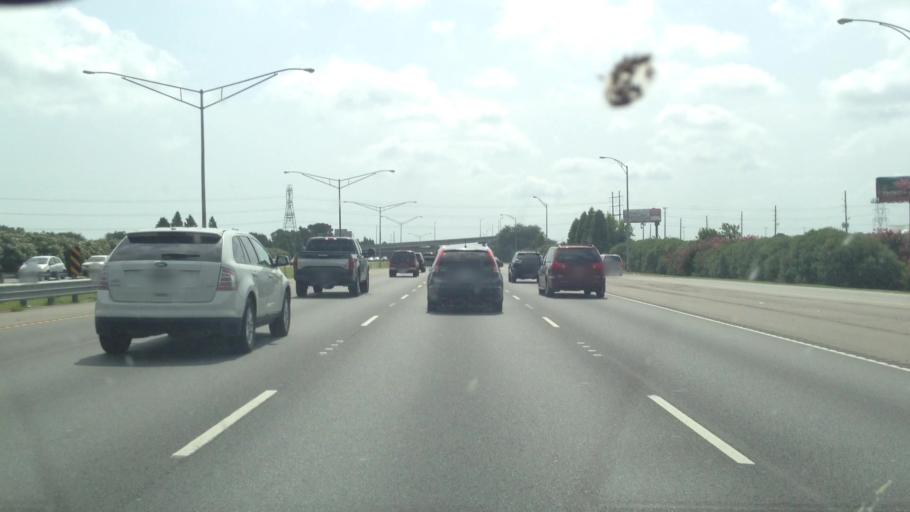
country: US
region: Louisiana
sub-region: Jefferson Parish
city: Kenner
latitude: 30.0085
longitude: -90.2281
